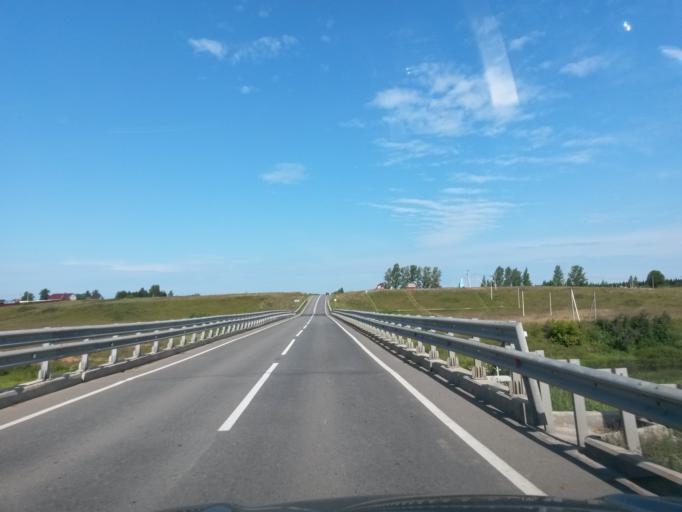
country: RU
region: Jaroslavl
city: Yaroslavl
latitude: 57.7863
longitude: 39.8371
